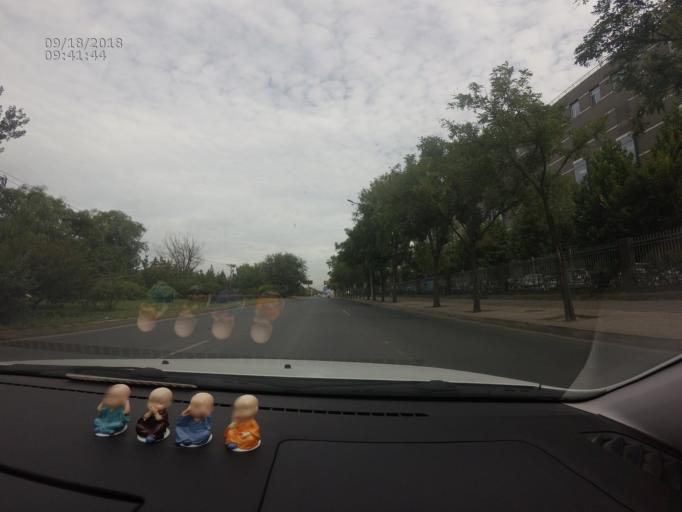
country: CN
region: Beijing
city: Xibeiwang
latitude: 40.0687
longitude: 116.2402
